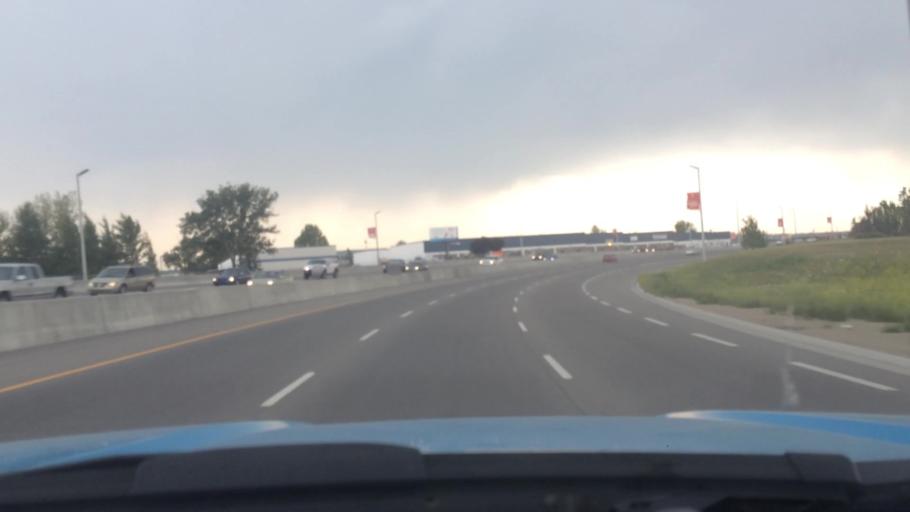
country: CA
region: Alberta
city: Calgary
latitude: 51.0930
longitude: -114.0237
